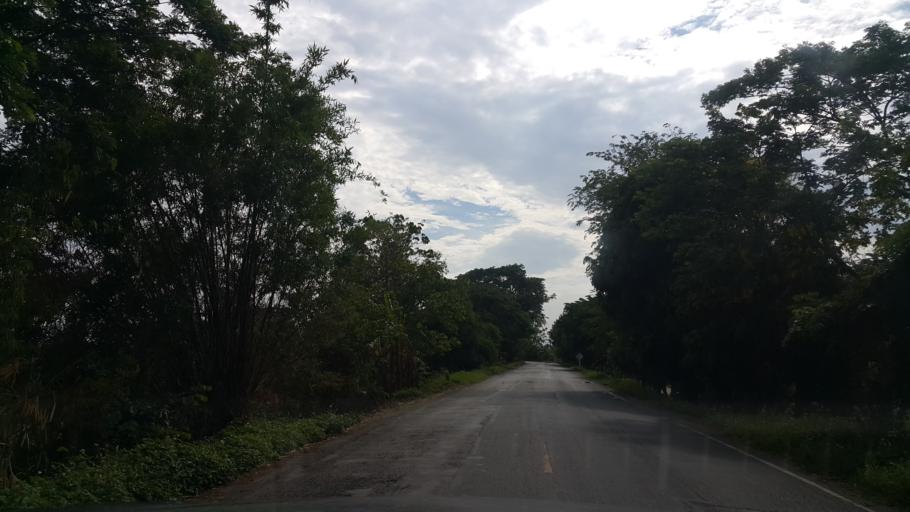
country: TH
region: Chiang Rai
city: Wiang Chai
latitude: 19.9598
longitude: 99.9411
